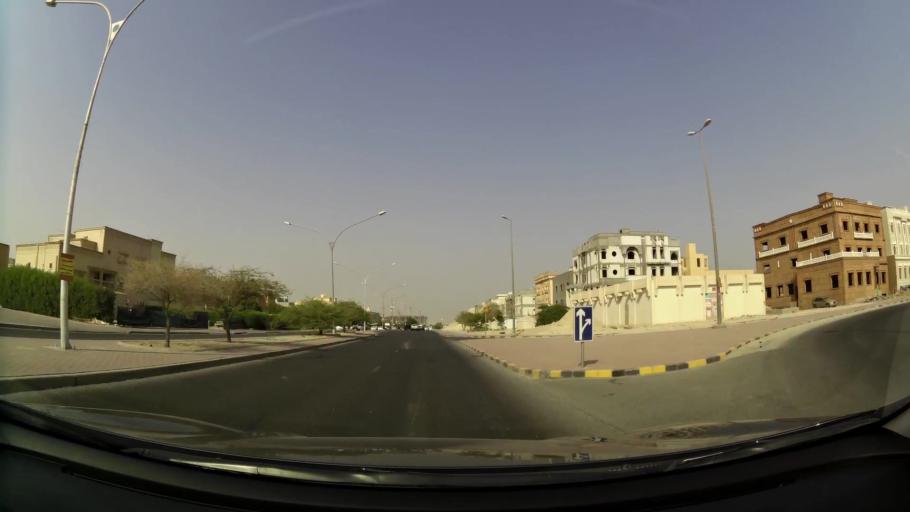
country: KW
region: Muhafazat al Jahra'
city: Al Jahra'
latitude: 29.3194
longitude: 47.6787
